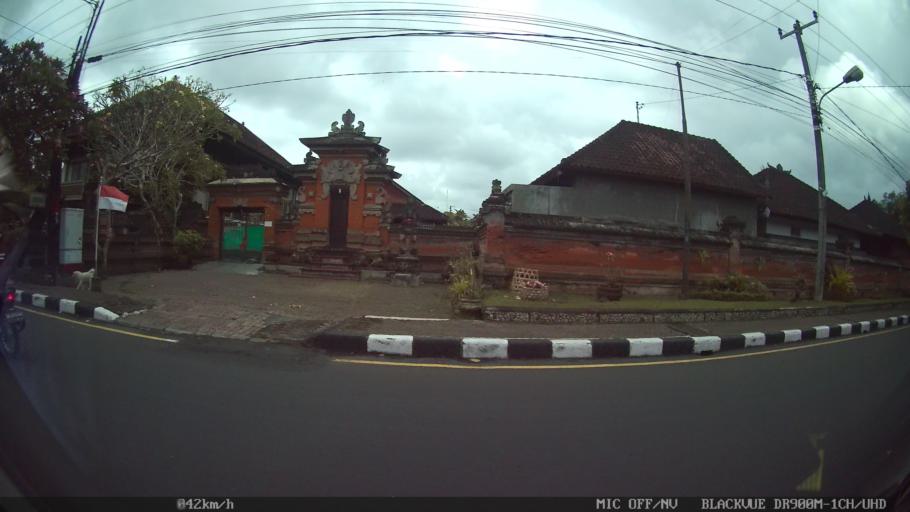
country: ID
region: Bali
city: Banjar Serangan
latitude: -8.5434
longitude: 115.1702
